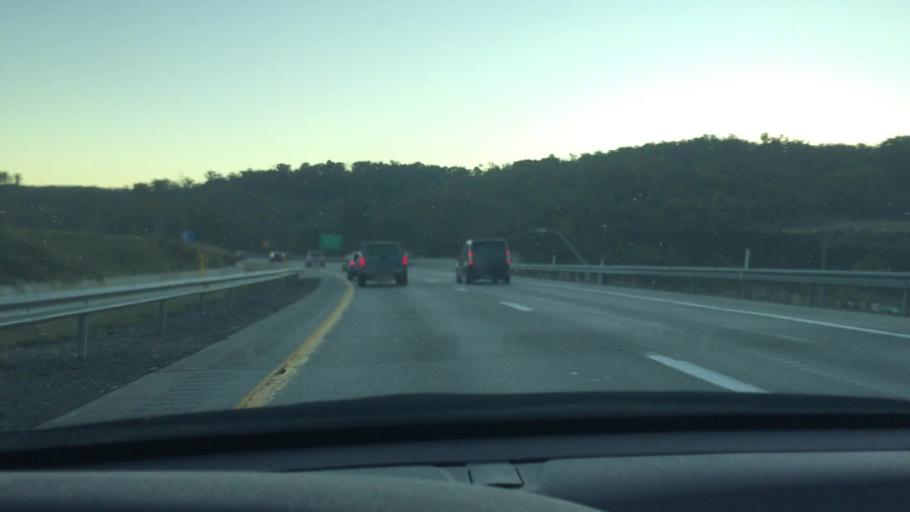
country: US
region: Pennsylvania
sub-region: Washington County
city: McGovern
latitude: 40.2107
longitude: -80.2266
